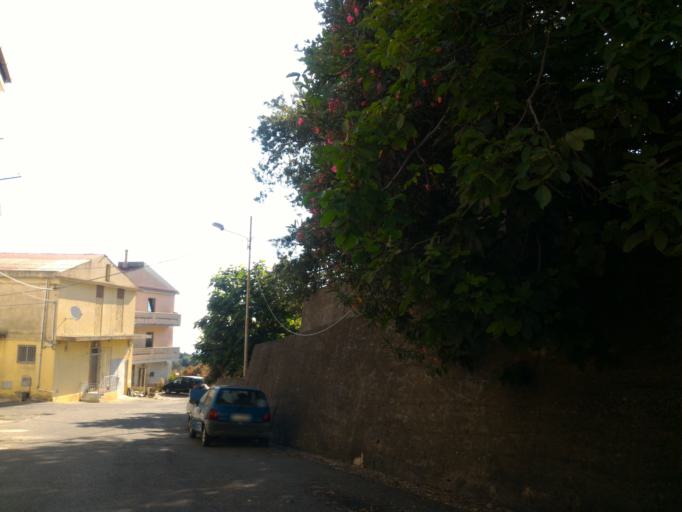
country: IT
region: Calabria
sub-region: Provincia di Crotone
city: Ciro
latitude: 39.3825
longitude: 17.0666
